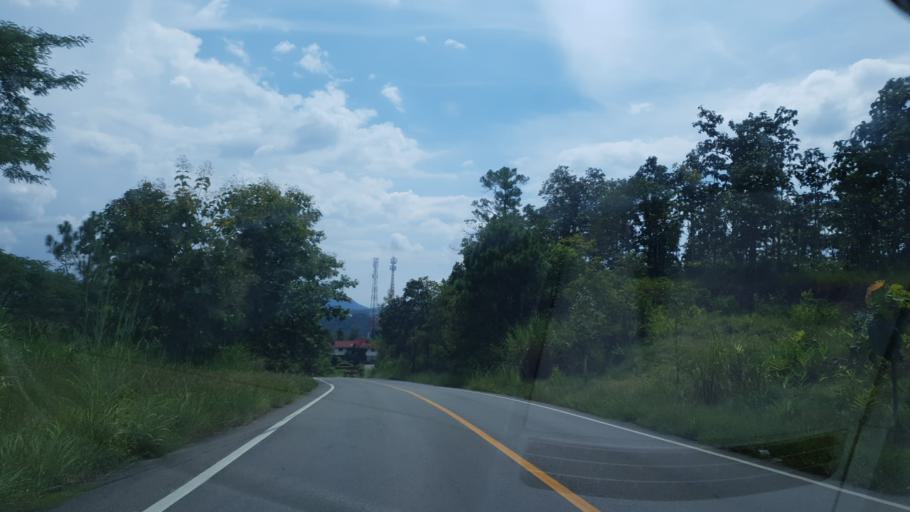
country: TH
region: Mae Hong Son
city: Khun Yuam
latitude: 18.7487
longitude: 97.9272
